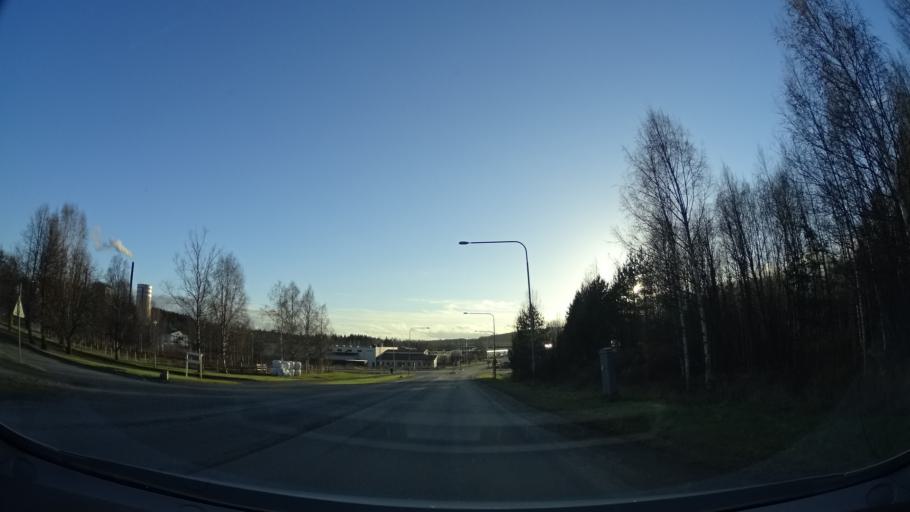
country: SE
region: Vaesterbotten
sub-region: Skelleftea Kommun
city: Soedra Bergsbyn
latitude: 64.7488
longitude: 21.0361
